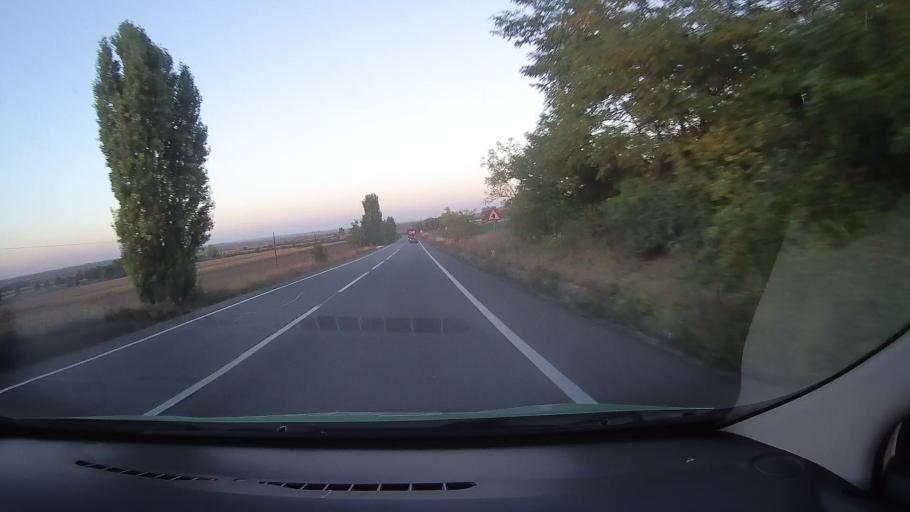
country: RO
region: Bihor
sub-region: Comuna Cherechiu
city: Cherechiu
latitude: 47.3805
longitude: 22.1411
